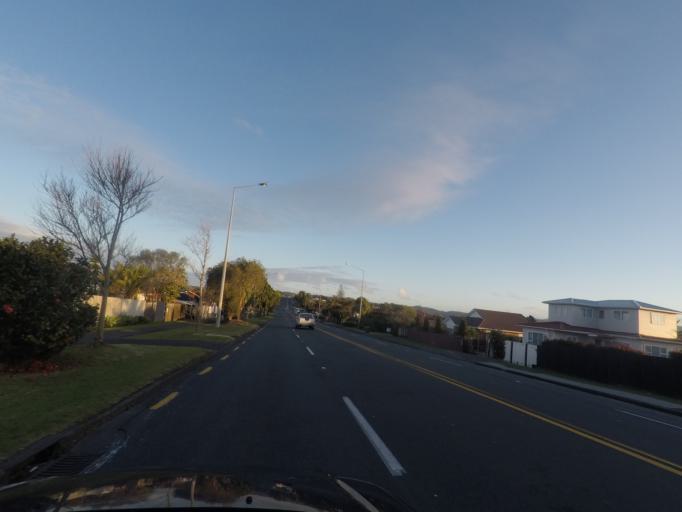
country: NZ
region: Auckland
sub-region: Auckland
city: Rosebank
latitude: -36.8876
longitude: 174.6445
